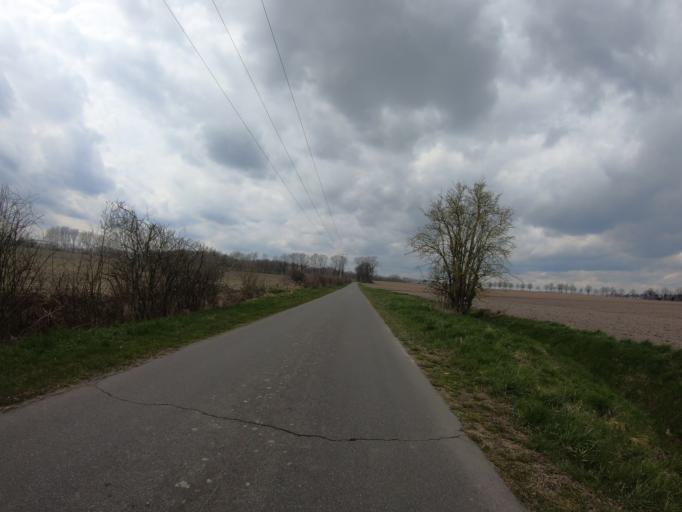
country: DE
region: Lower Saxony
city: Hankensbuttel
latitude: 52.7284
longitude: 10.6388
